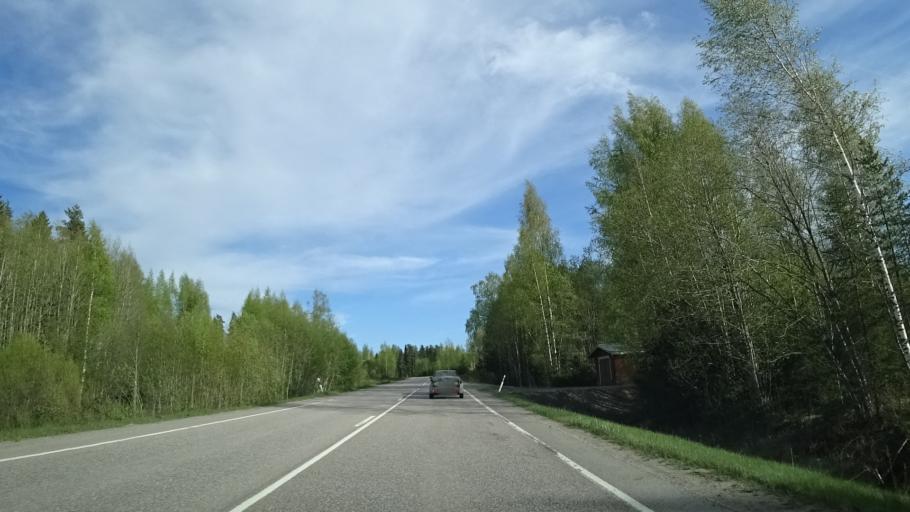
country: FI
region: Haeme
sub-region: Riihimaeki
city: Loppi
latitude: 60.5952
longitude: 24.4971
